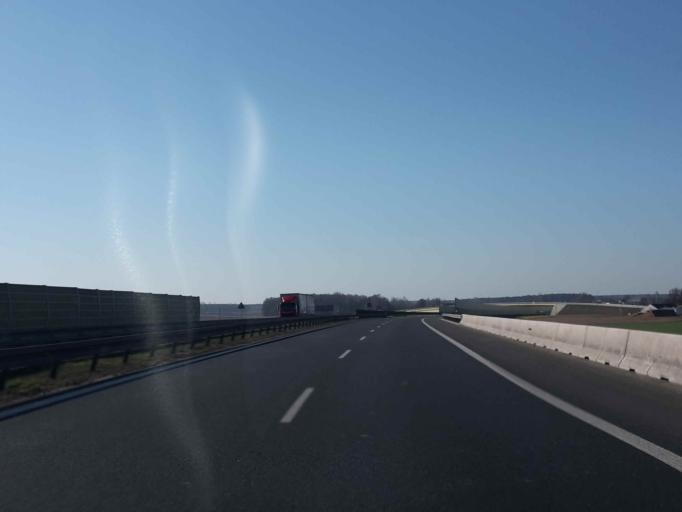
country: PL
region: Greater Poland Voivodeship
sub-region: Powiat gnieznienski
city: Lubowo
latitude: 52.5034
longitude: 17.4655
